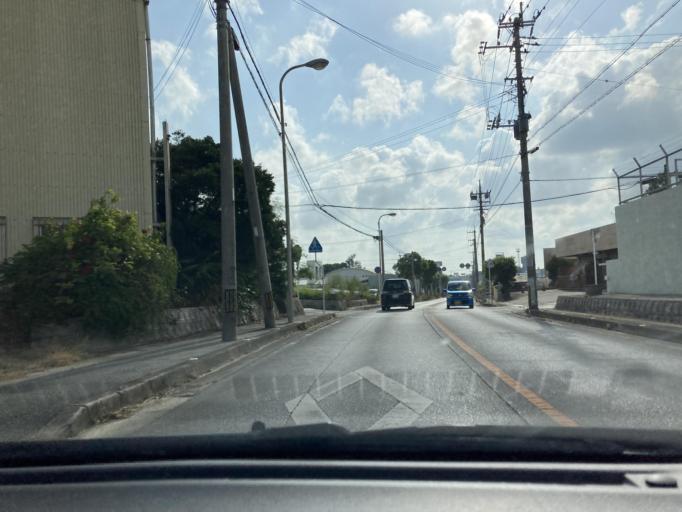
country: JP
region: Okinawa
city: Tomigusuku
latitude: 26.1576
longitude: 127.7271
